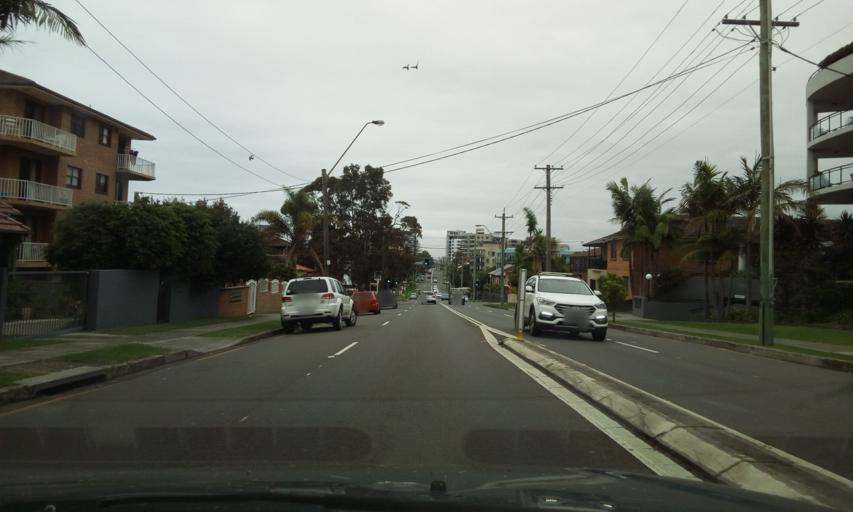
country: AU
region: New South Wales
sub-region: Wollongong
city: Wollongong
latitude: -34.4196
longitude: 150.9011
